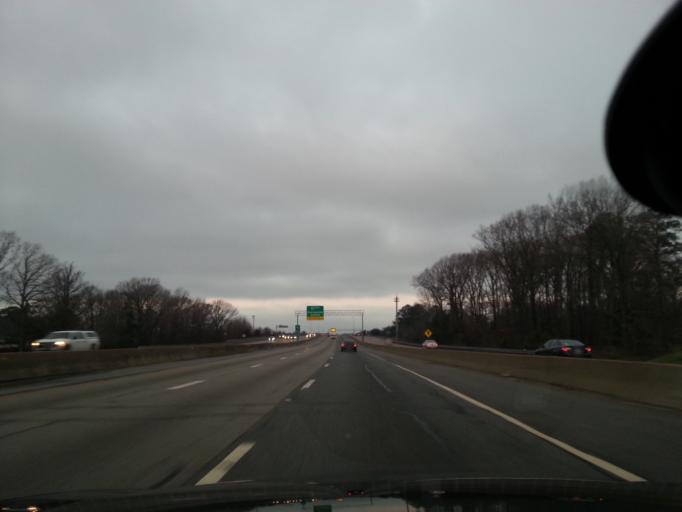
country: US
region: Virginia
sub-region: City of Chesapeake
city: Chesapeake
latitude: 36.8461
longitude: -76.1779
